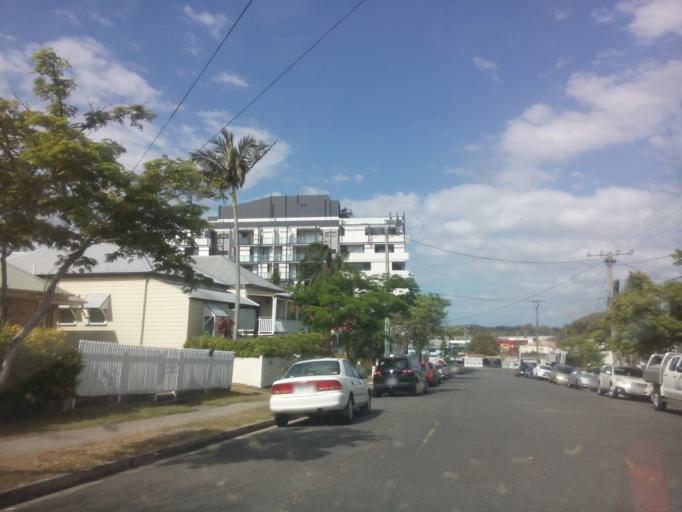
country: AU
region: Queensland
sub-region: Brisbane
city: Woolloongabba
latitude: -27.4926
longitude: 153.0396
